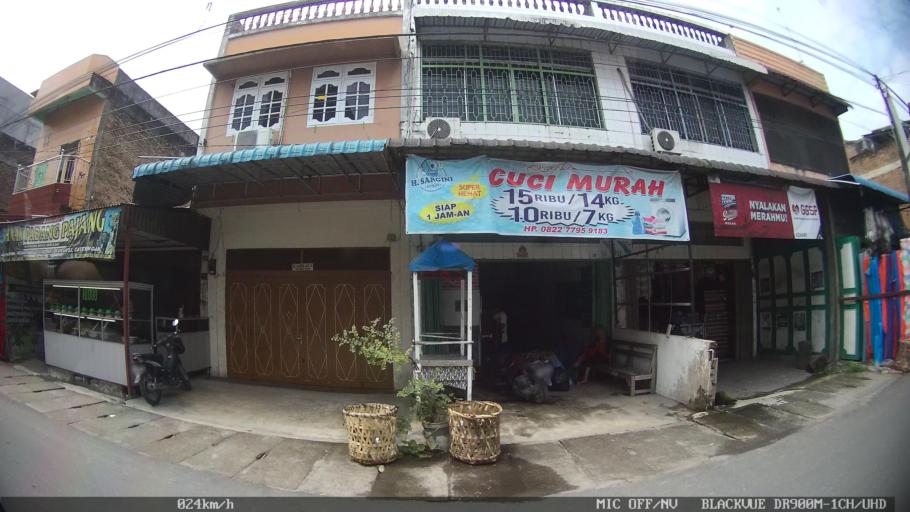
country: ID
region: North Sumatra
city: Percut
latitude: 3.6132
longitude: 98.8011
